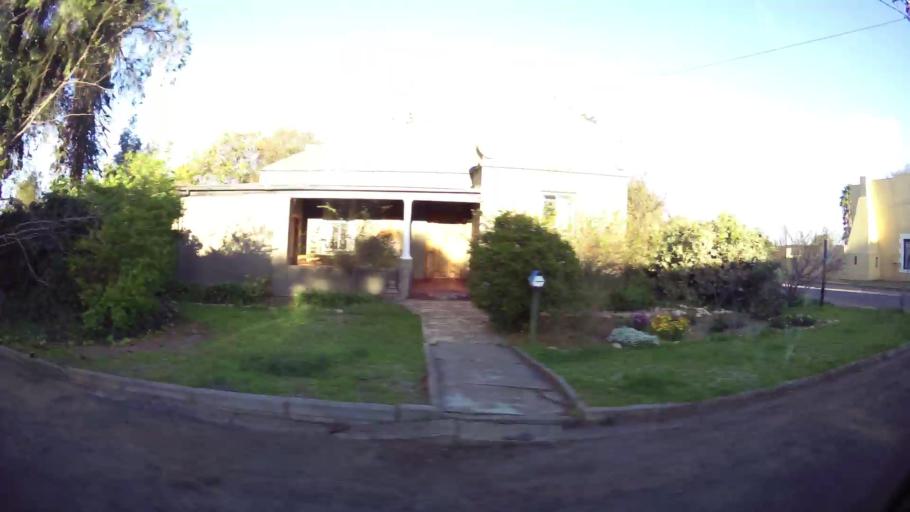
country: ZA
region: Western Cape
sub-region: Eden District Municipality
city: Riversdale
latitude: -34.0866
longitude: 20.9615
